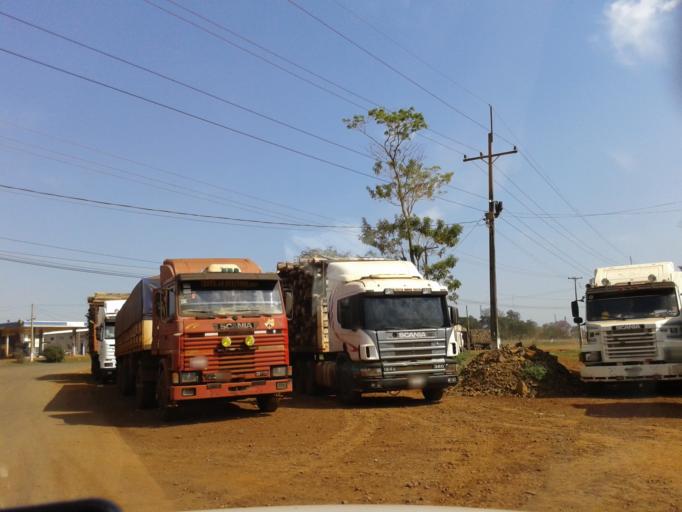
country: PY
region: Alto Parana
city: Colonia Yguazu
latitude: -25.4852
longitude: -54.8804
